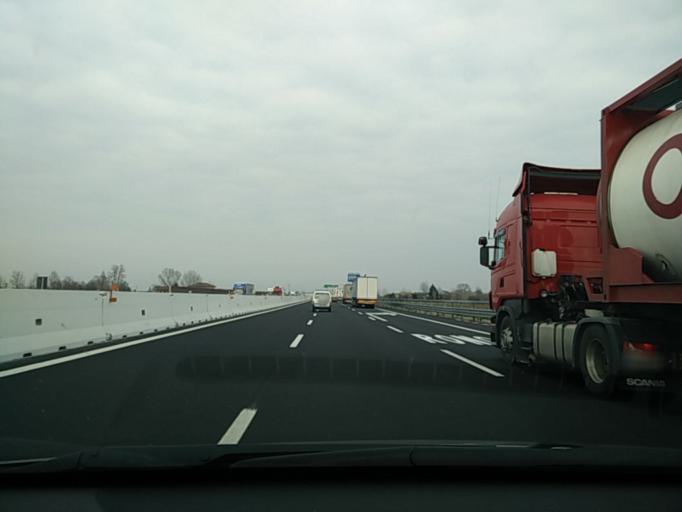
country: IT
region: Veneto
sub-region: Provincia di Venezia
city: Meolo
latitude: 45.6227
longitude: 12.4284
